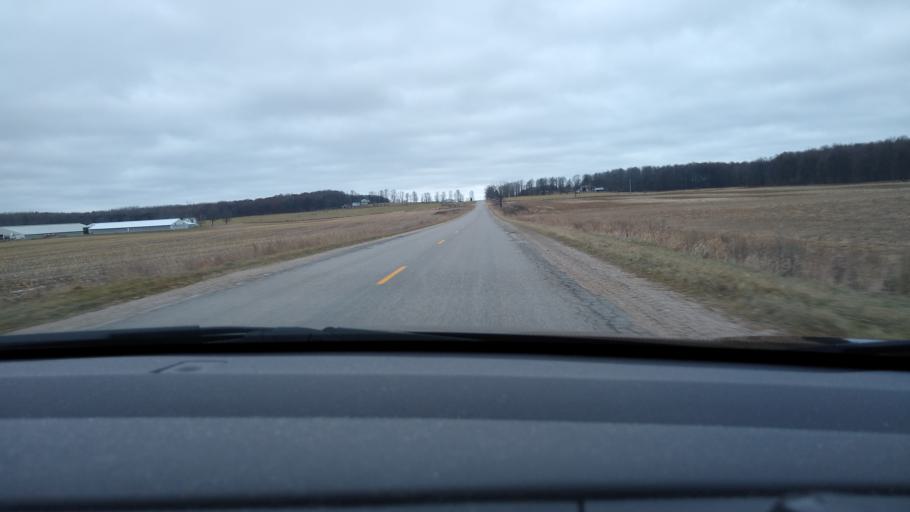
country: US
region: Michigan
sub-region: Missaukee County
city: Lake City
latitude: 44.3173
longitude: -85.0546
